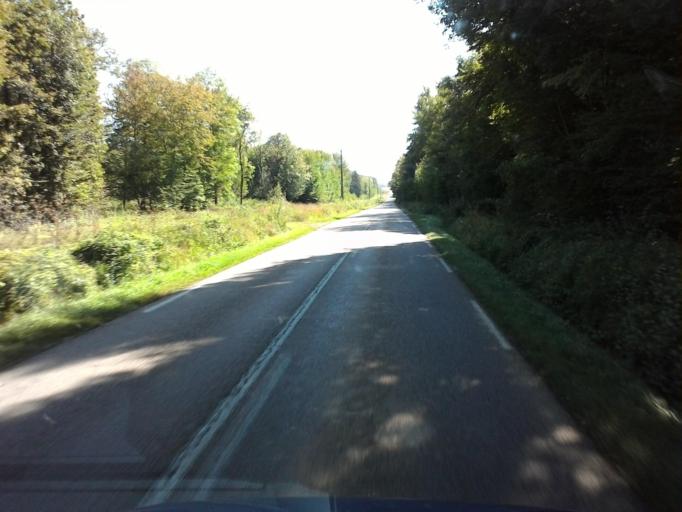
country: FR
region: Bourgogne
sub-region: Departement de l'Yonne
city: Joux-la-Ville
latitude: 47.5882
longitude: 3.8695
